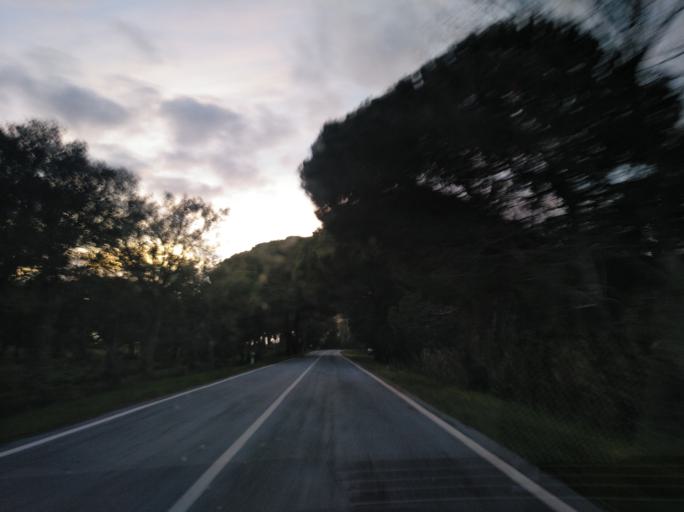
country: PT
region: Setubal
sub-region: Grandola
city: Grandola
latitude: 38.2007
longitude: -8.6201
